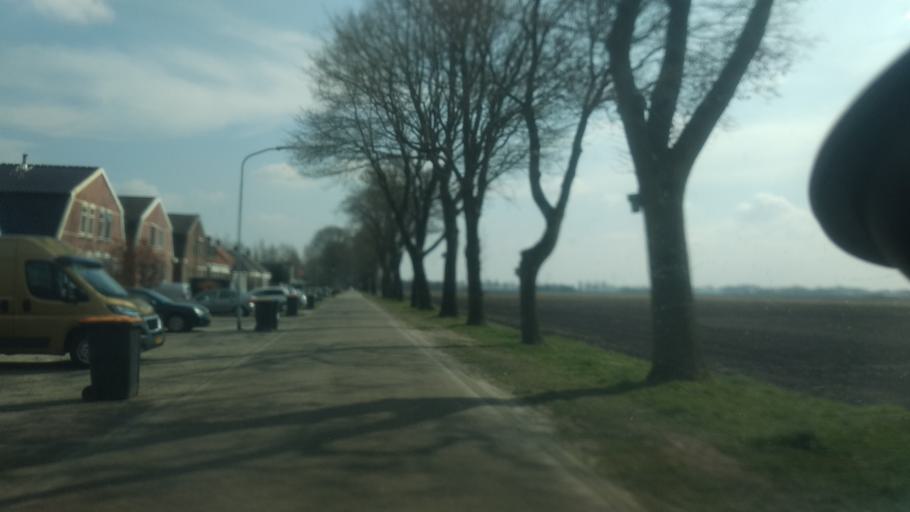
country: NL
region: Groningen
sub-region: Gemeente Stadskanaal
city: Stadskanaal
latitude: 52.9977
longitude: 6.9255
